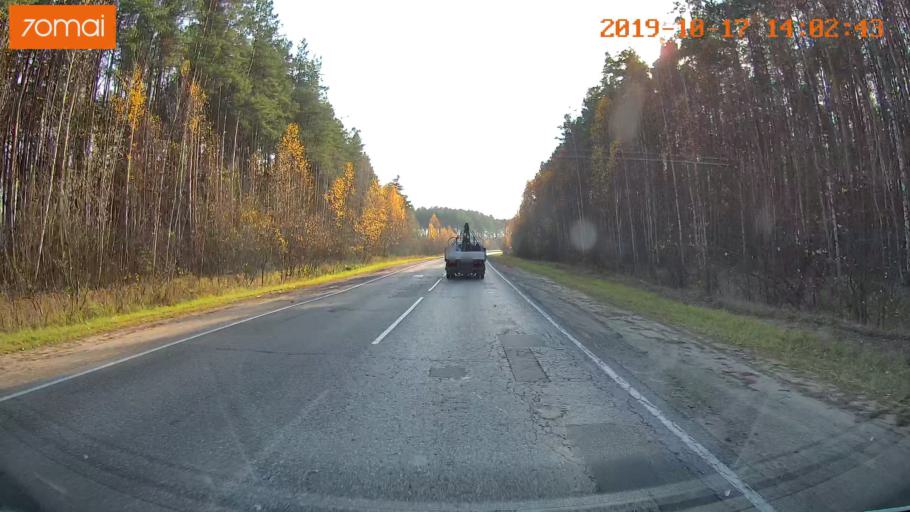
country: RU
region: Rjazan
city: Spas-Klepiki
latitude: 55.1436
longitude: 40.1496
